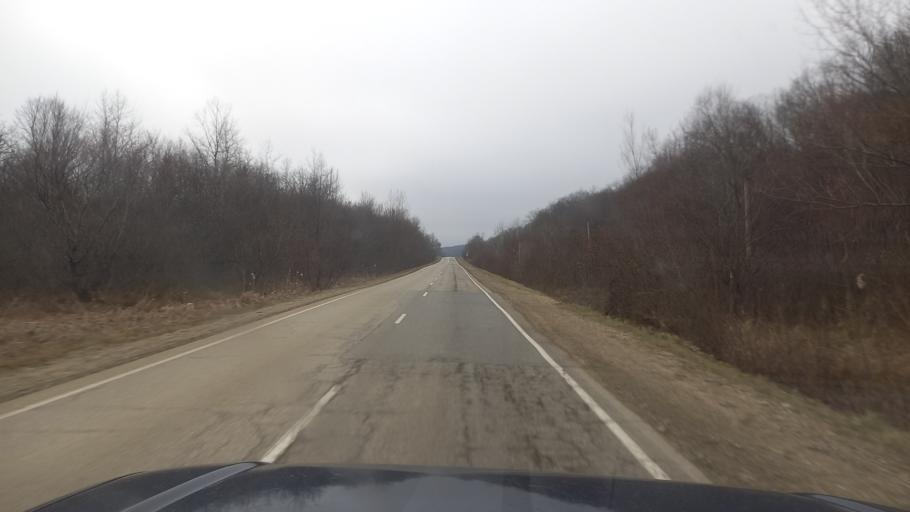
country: RU
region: Krasnodarskiy
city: Neftegorsk
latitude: 44.2795
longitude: 39.7957
